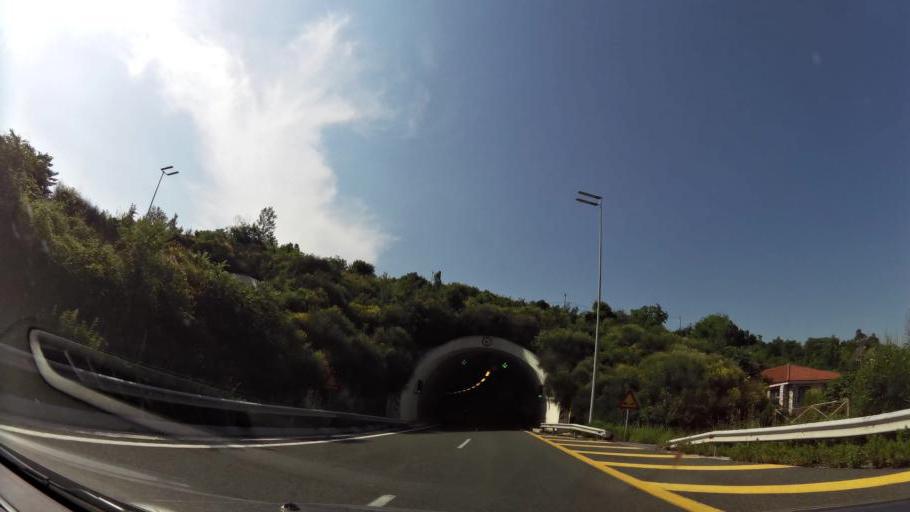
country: GR
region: Central Macedonia
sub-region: Nomos Imathias
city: Rizomata
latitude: 40.4313
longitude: 22.1831
